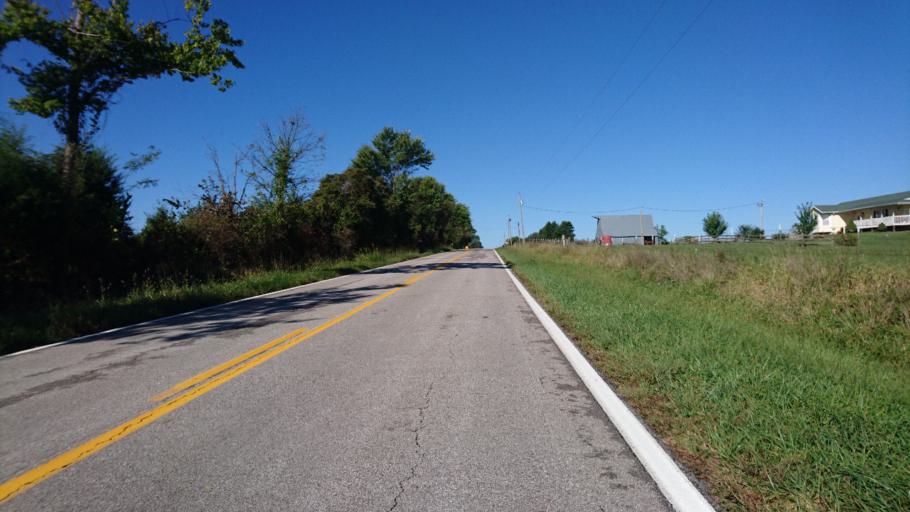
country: US
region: Missouri
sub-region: Greene County
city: Ash Grove
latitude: 37.1938
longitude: -93.6504
